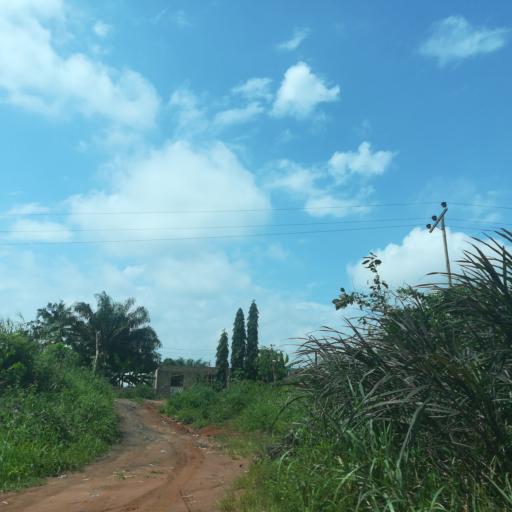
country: NG
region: Lagos
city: Ikorodu
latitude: 6.6597
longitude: 3.6824
